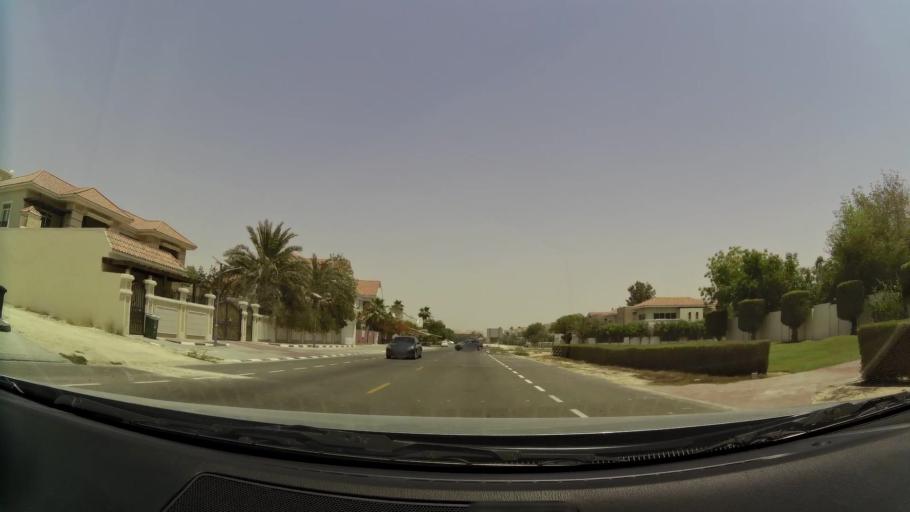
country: AE
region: Dubai
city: Dubai
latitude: 25.1617
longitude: 55.2165
